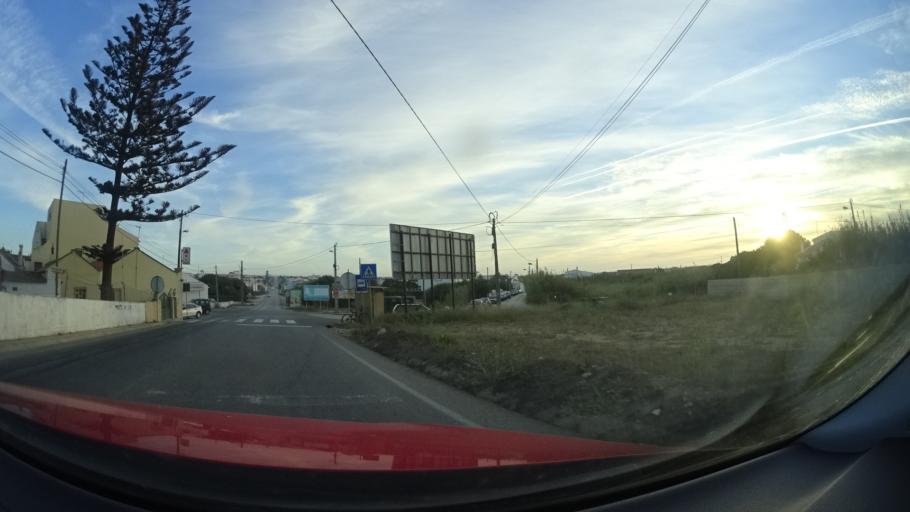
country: PT
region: Faro
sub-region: Vila do Bispo
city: Sagres
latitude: 37.0195
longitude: -8.9393
